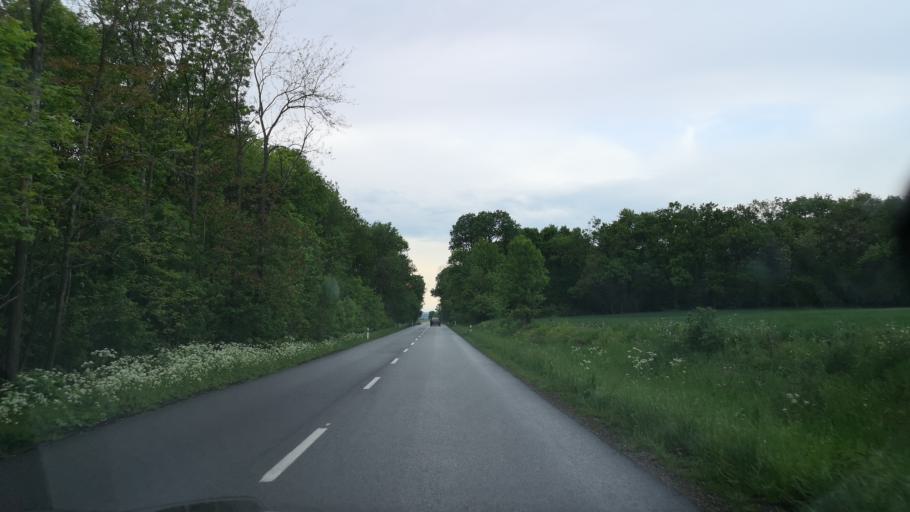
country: SK
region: Nitriansky
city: Sellye
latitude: 48.2271
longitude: 17.9680
